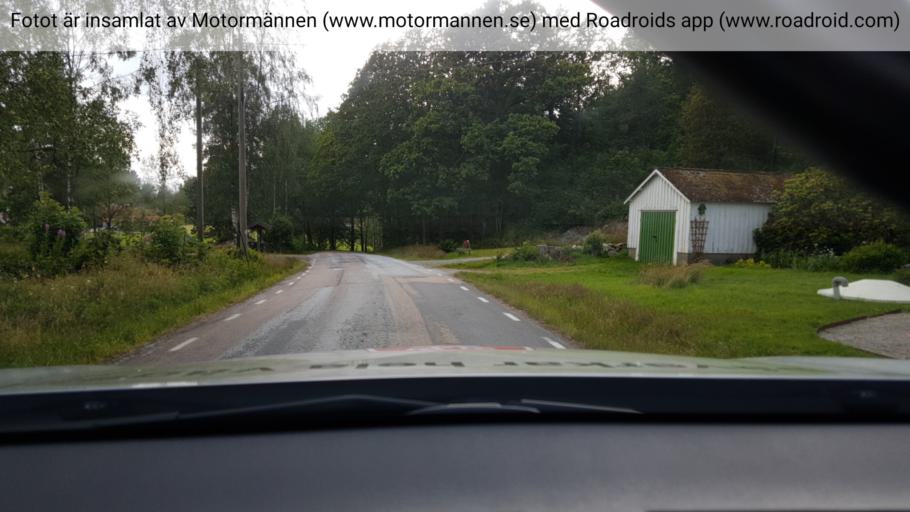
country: SE
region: Vaestra Goetaland
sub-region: Orust
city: Henan
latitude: 58.1578
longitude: 11.6474
